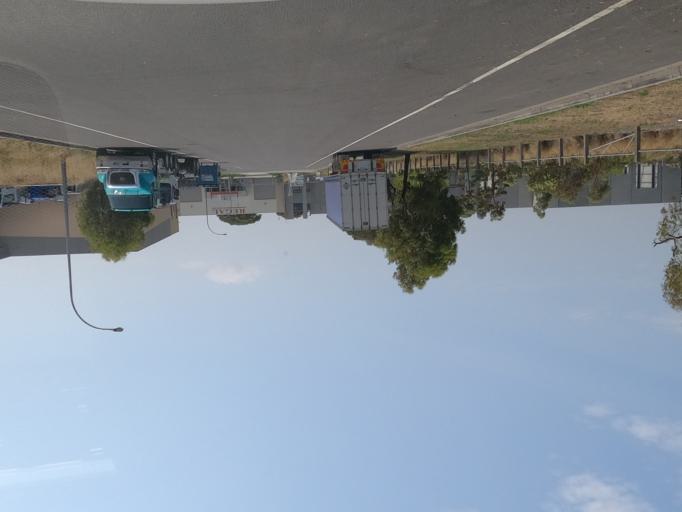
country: AU
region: Victoria
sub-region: Hume
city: Craigieburn
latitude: -37.6160
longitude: 144.9420
